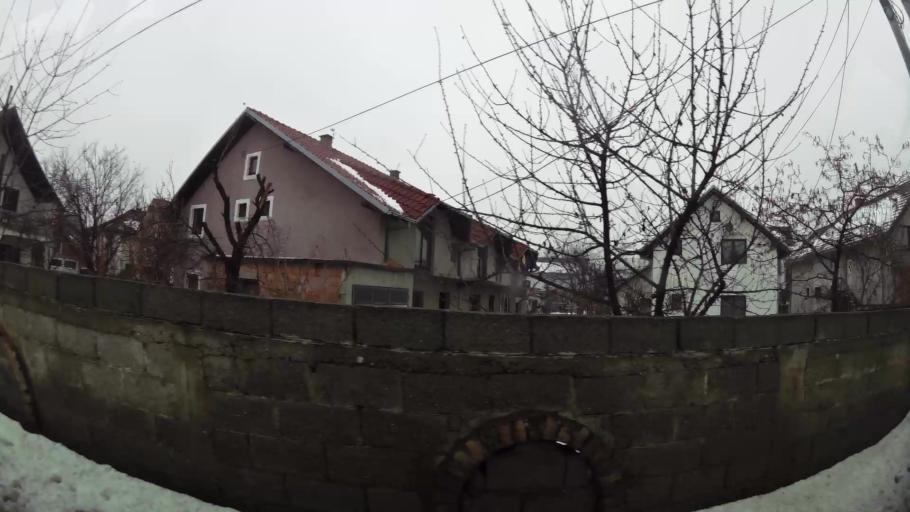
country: RS
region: Central Serbia
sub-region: Belgrade
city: Zemun
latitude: 44.8473
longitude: 20.3611
